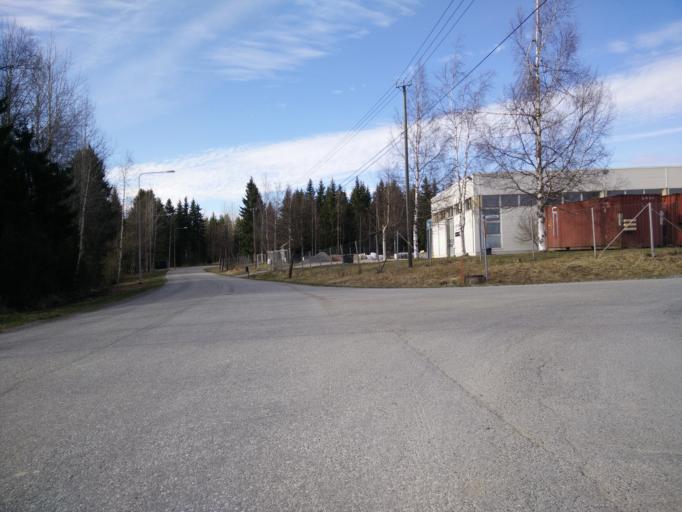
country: FI
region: Pirkanmaa
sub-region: Tampere
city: Orivesi
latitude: 61.6900
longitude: 24.3646
